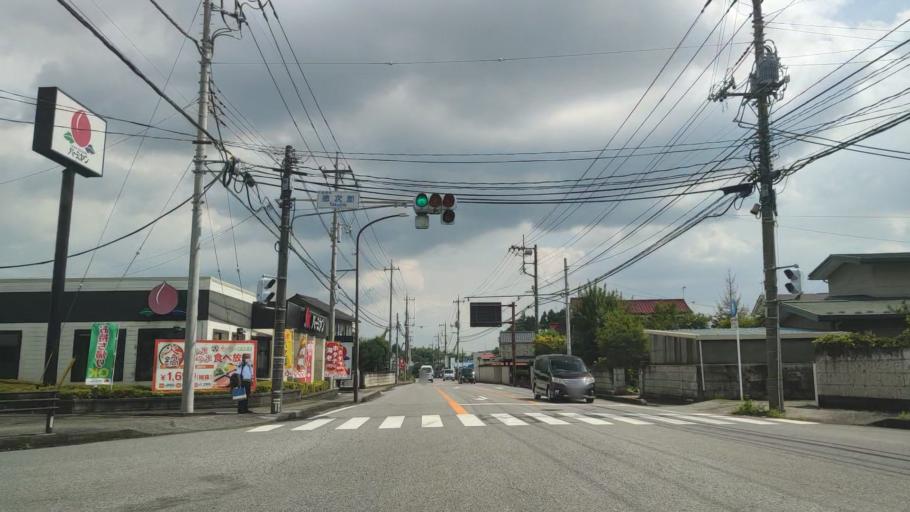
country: JP
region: Tochigi
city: Utsunomiya-shi
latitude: 36.6504
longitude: 139.8442
